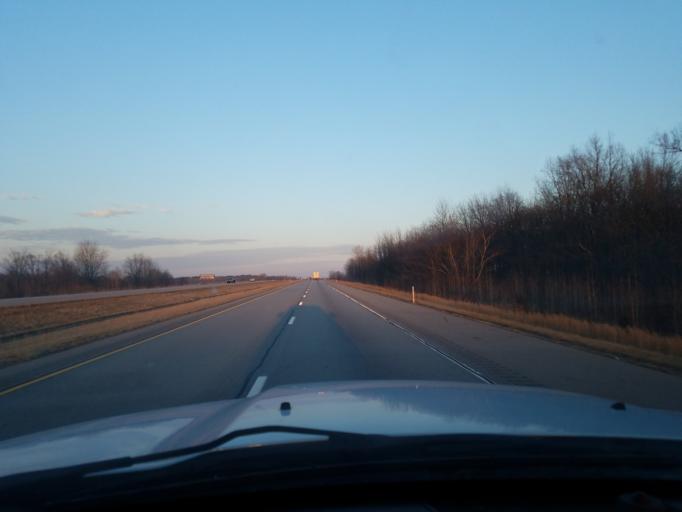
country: US
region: Indiana
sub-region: Warrick County
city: Chandler
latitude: 38.1878
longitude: -87.3539
